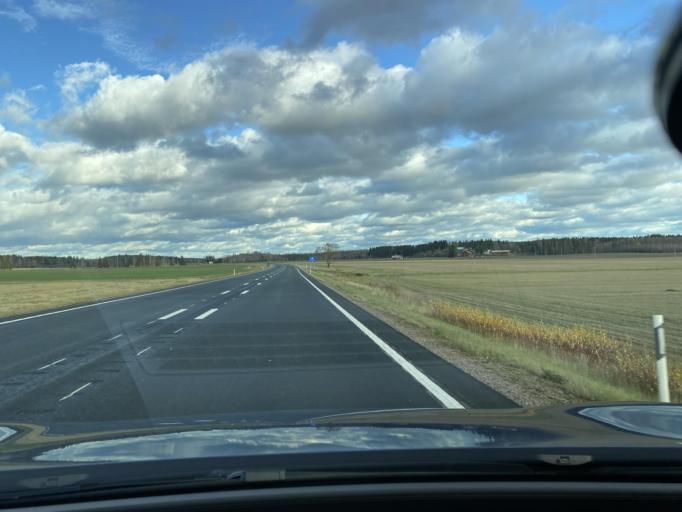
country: FI
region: Haeme
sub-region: Riihimaeki
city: Oitti
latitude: 60.8389
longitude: 25.1033
